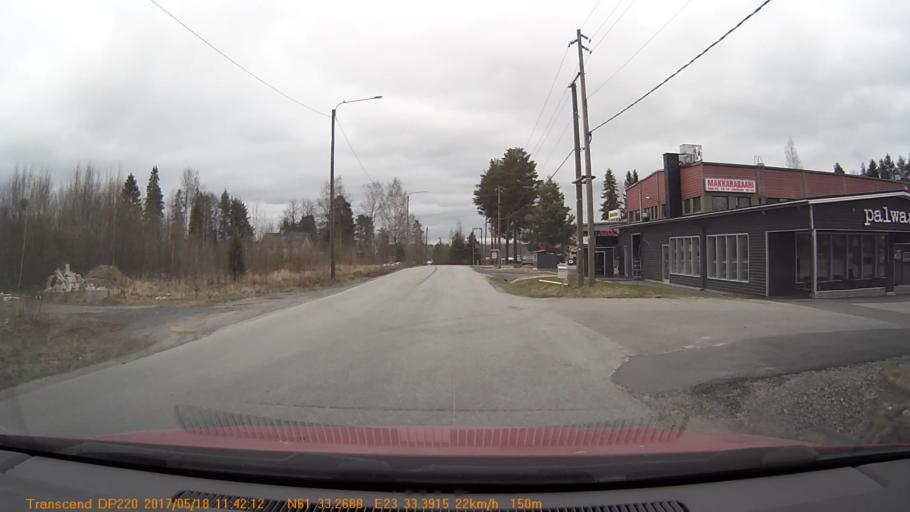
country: FI
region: Pirkanmaa
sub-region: Tampere
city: Yloejaervi
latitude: 61.5546
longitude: 23.5566
